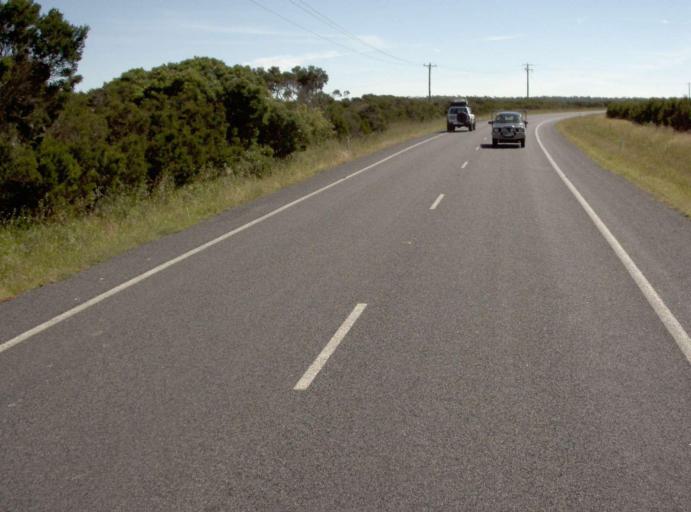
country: AU
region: Victoria
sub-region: Latrobe
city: Traralgon
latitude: -38.6342
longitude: 146.5855
